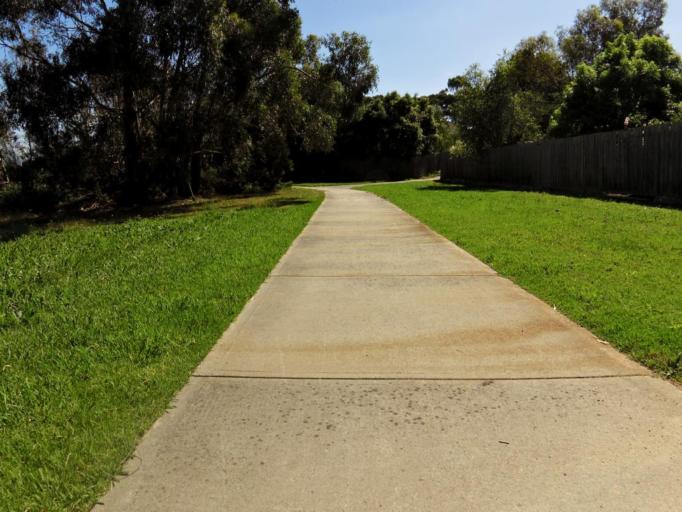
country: AU
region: Victoria
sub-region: Casey
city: Endeavour Hills
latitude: -37.9570
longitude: 145.2686
